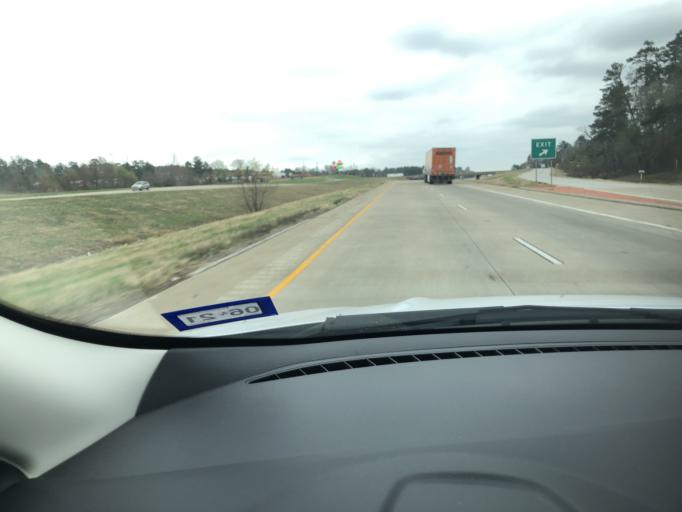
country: US
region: Texas
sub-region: Angelina County
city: Redland
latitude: 31.4154
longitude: -94.7218
